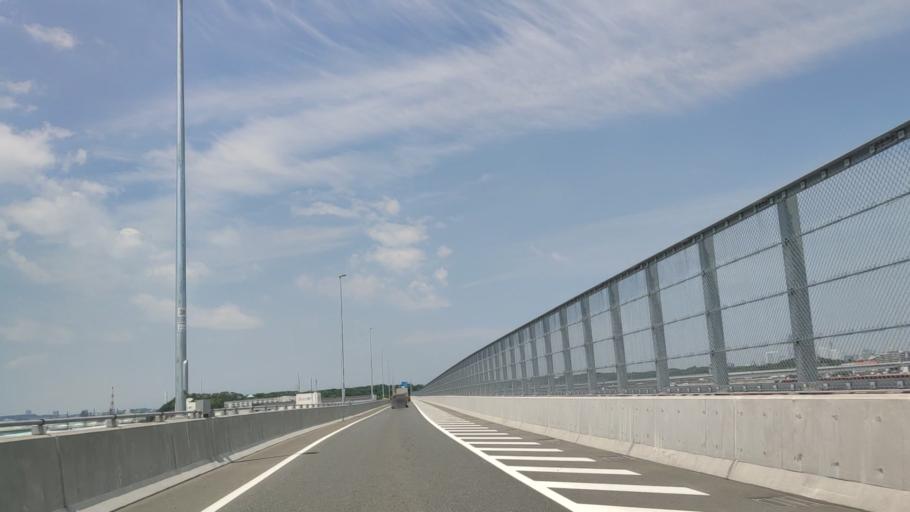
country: JP
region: Kanagawa
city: Yokohama
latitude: 35.4136
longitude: 139.6763
